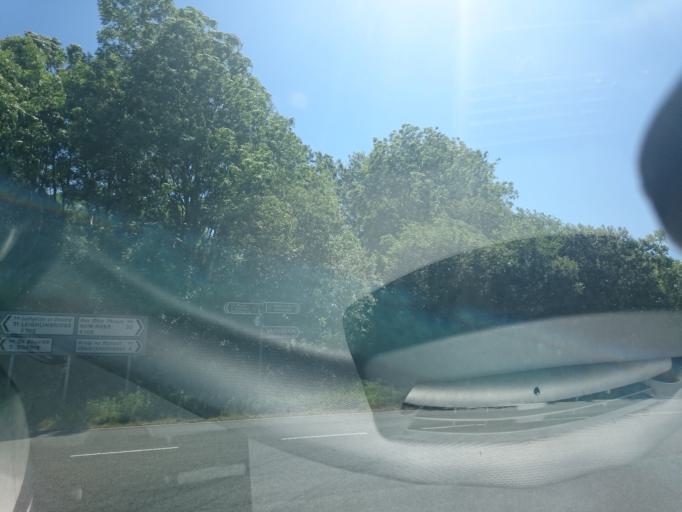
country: IE
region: Leinster
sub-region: Kilkenny
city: Graiguenamanagh
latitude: 52.5789
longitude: -6.9518
